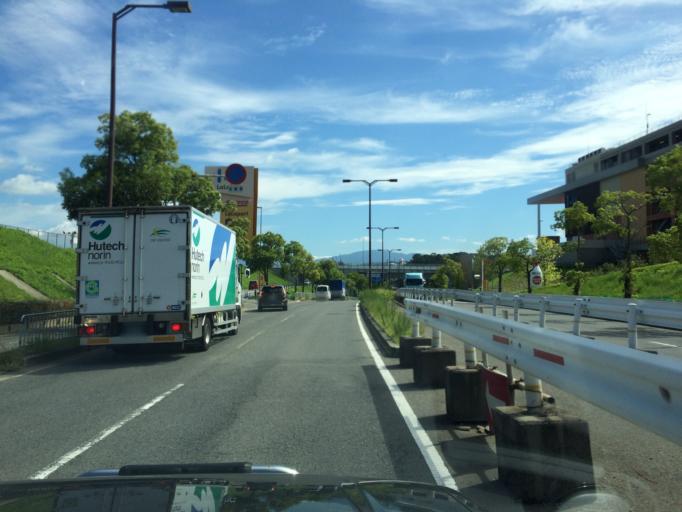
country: JP
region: Osaka
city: Izumi
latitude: 34.4387
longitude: 135.4469
